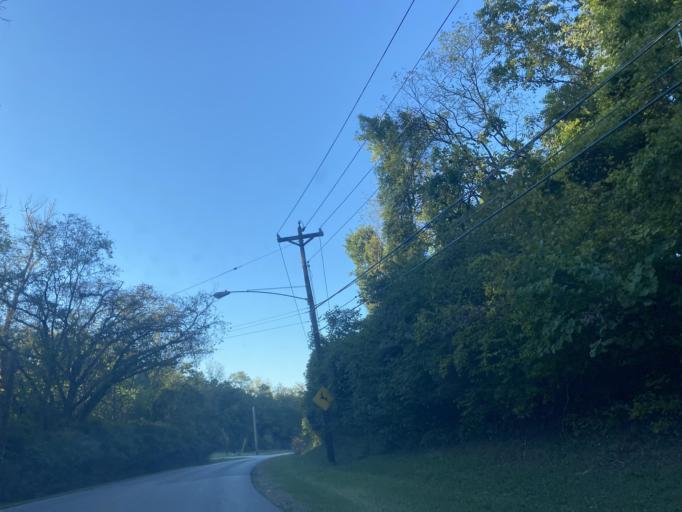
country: US
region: Kentucky
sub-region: Campbell County
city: Dayton
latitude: 39.1090
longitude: -84.4657
